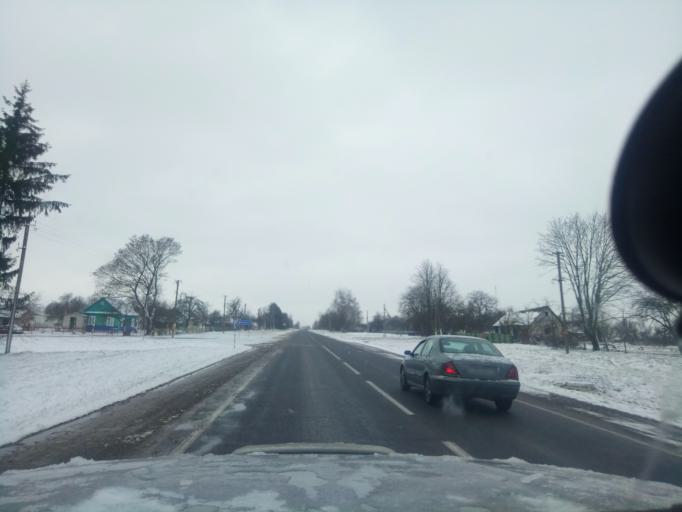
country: BY
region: Minsk
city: Klyetsk
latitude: 53.1240
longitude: 26.6678
